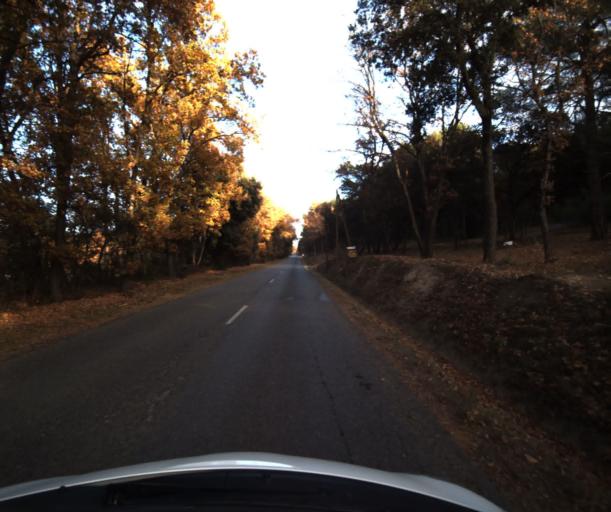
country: FR
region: Provence-Alpes-Cote d'Azur
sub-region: Departement du Vaucluse
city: Pertuis
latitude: 43.6968
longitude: 5.5417
